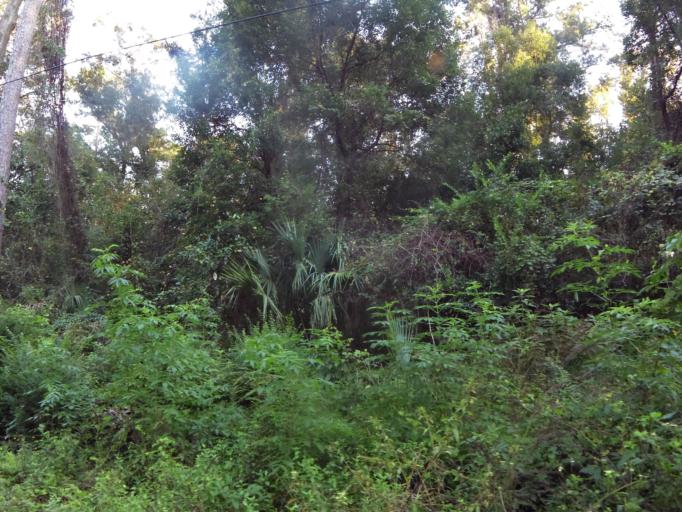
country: US
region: Florida
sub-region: Duval County
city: Jacksonville
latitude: 30.3656
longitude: -81.7356
